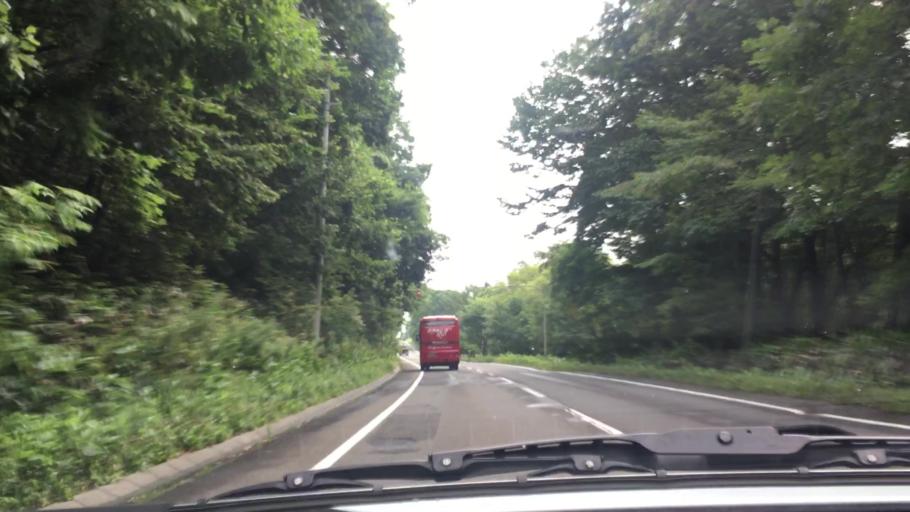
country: JP
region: Hokkaido
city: Chitose
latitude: 42.9434
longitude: 141.7482
